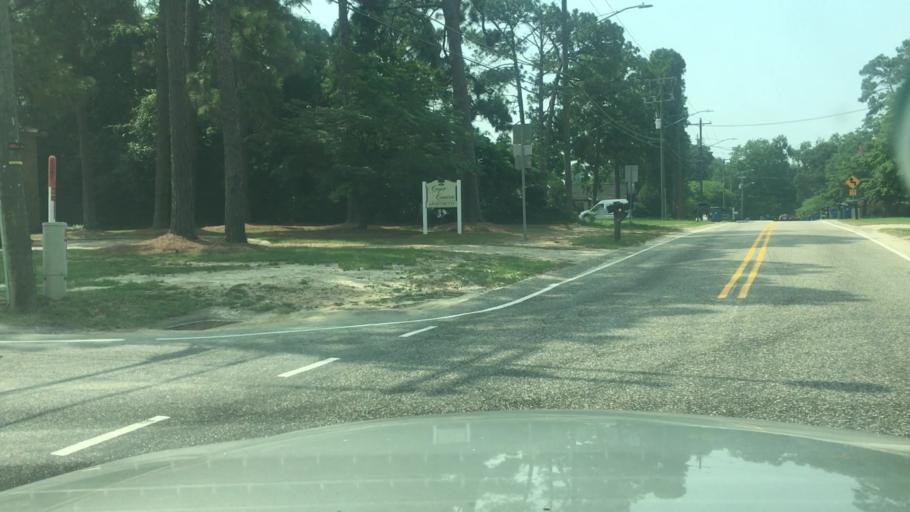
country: US
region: North Carolina
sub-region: Cumberland County
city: Fayetteville
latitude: 35.0363
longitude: -78.9411
